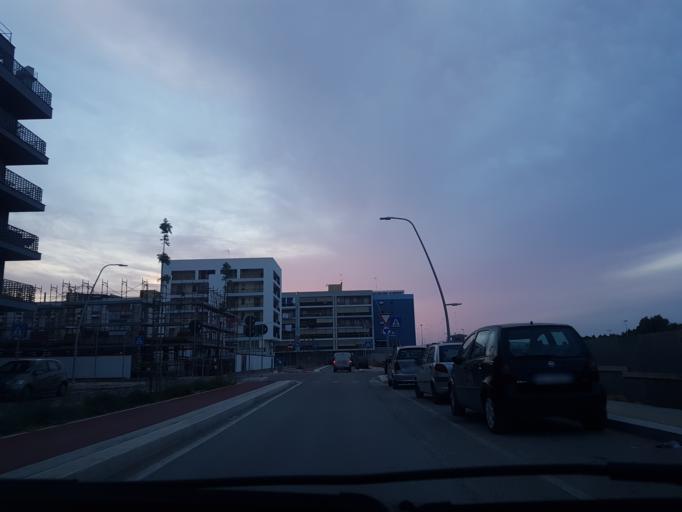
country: IT
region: Apulia
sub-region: Provincia di Barletta - Andria - Trani
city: Barletta
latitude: 41.3061
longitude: 16.2666
